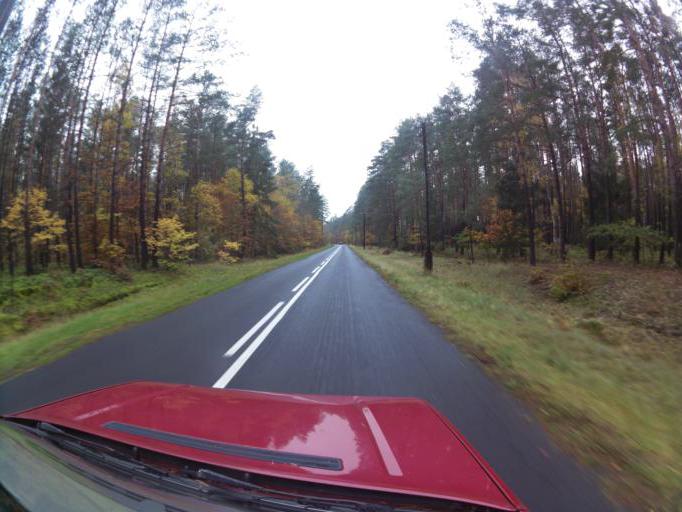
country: PL
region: West Pomeranian Voivodeship
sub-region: Powiat policki
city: Dobra
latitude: 53.5973
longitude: 14.3459
